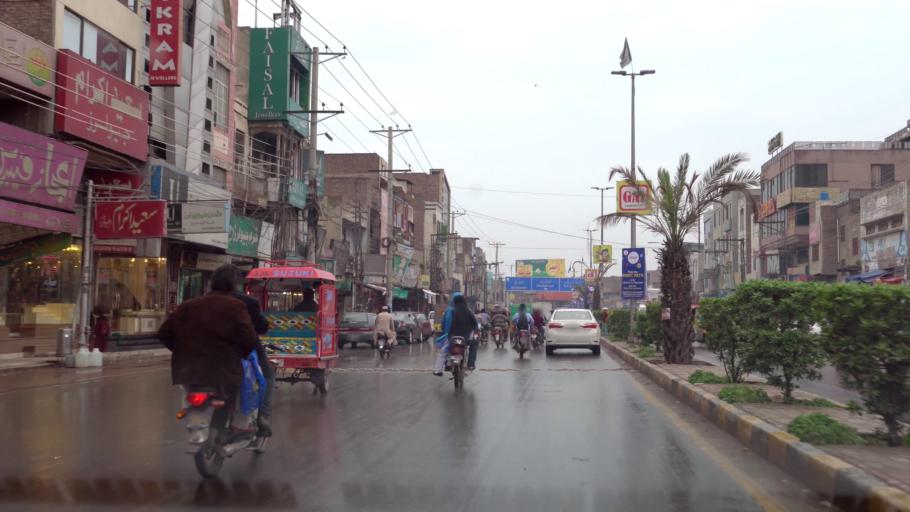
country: PK
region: Punjab
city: Faisalabad
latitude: 31.4075
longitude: 73.0990
